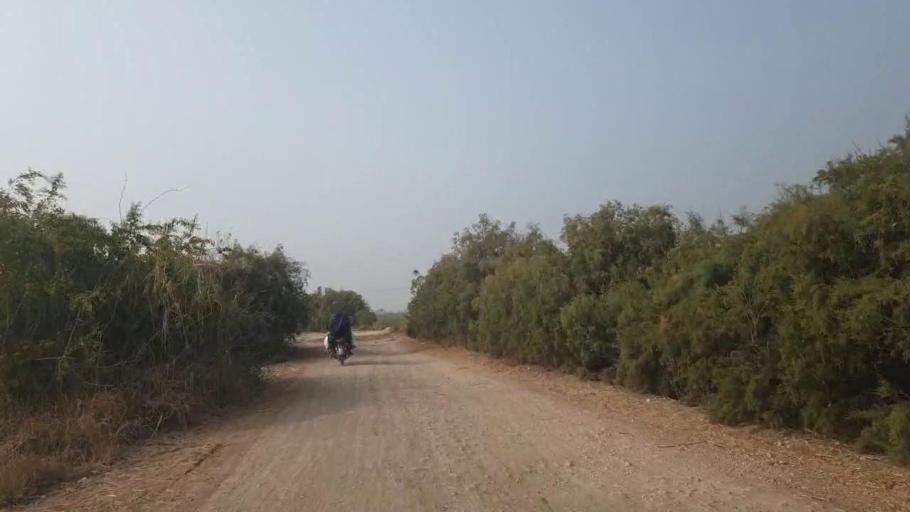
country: PK
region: Sindh
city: Bhit Shah
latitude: 25.8551
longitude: 68.5645
